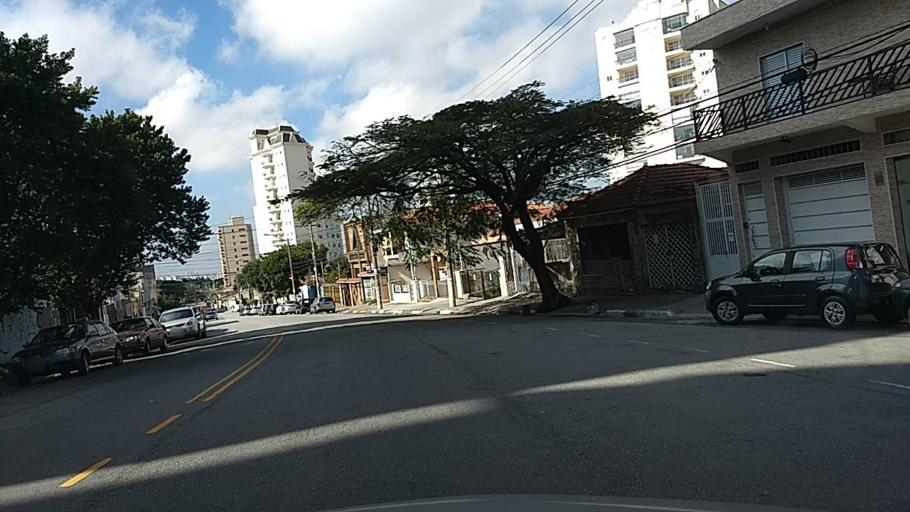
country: BR
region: Sao Paulo
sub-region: Sao Paulo
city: Sao Paulo
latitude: -23.5102
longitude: -46.5856
